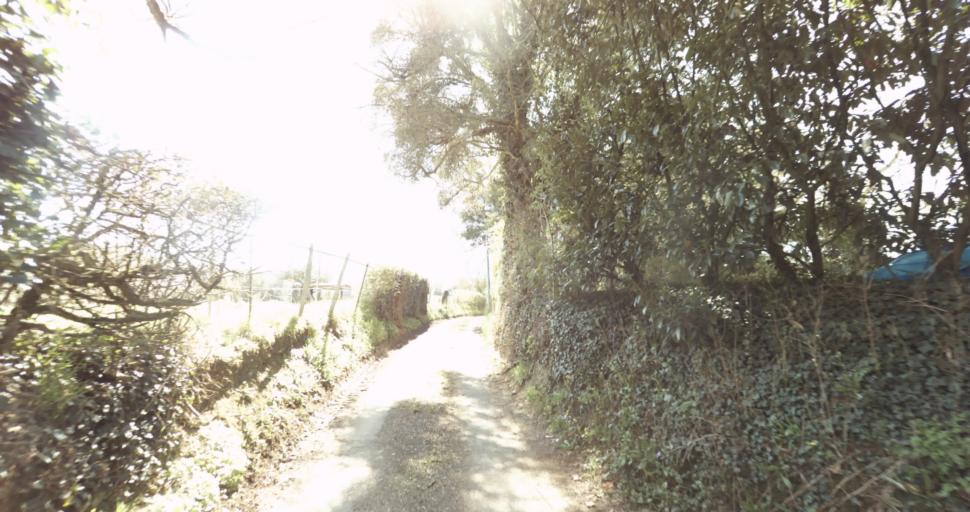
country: FR
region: Lower Normandy
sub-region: Departement du Calvados
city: Saint-Pierre-sur-Dives
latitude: 49.0165
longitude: 0.0443
